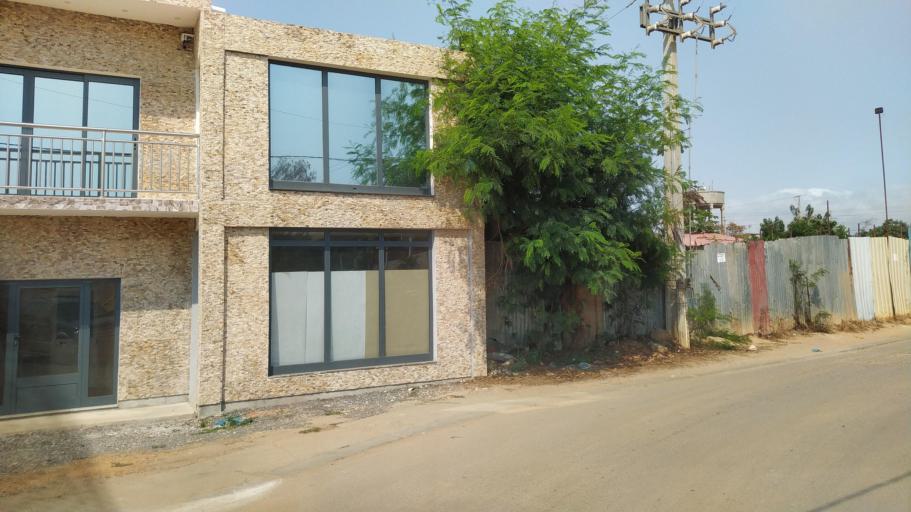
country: AO
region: Luanda
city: Luanda
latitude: -8.9062
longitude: 13.2296
